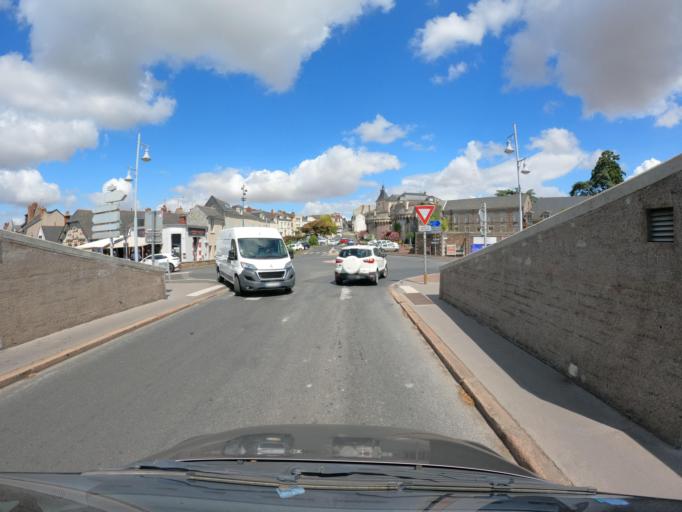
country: FR
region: Pays de la Loire
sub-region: Departement de la Loire-Atlantique
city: Ancenis
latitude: 47.3634
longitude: -1.1772
